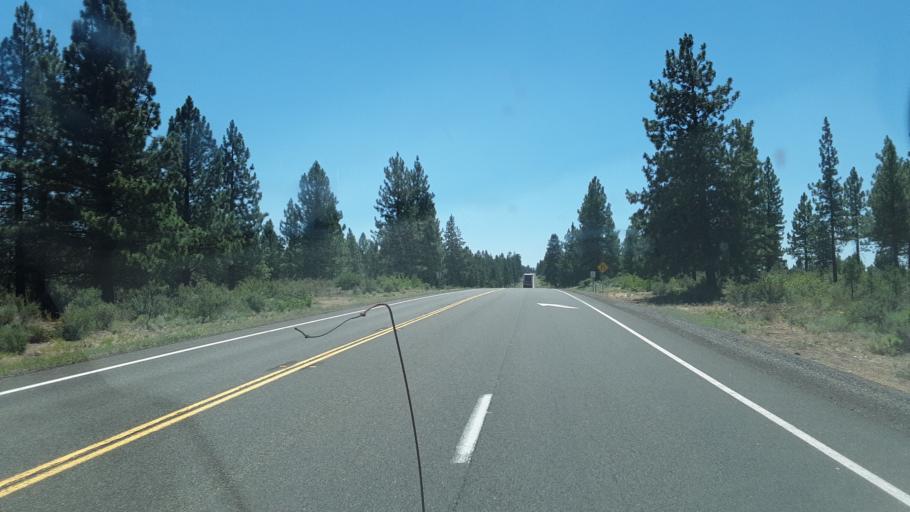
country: US
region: California
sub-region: Siskiyou County
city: Tulelake
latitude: 41.6024
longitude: -121.2059
